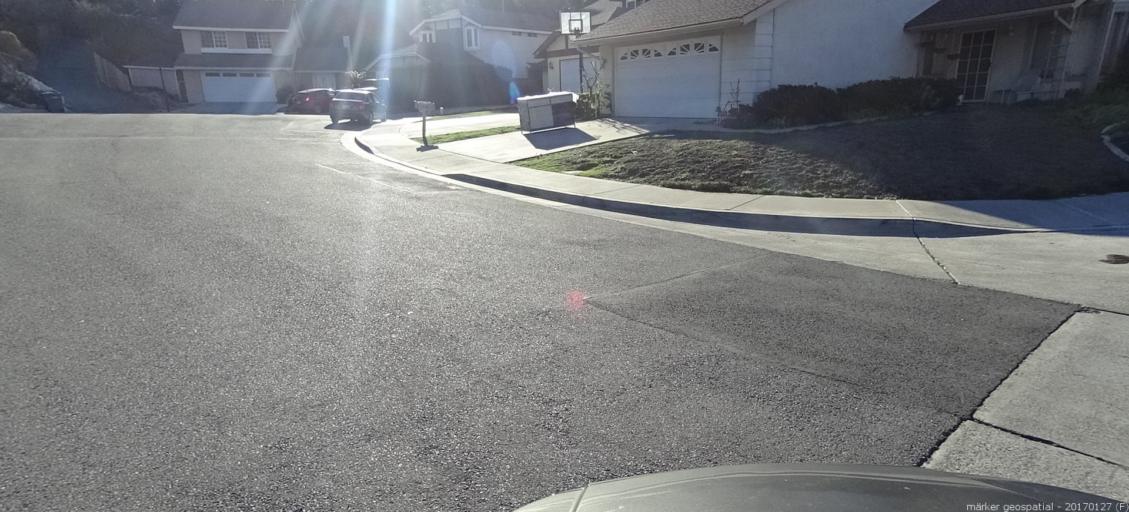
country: US
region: California
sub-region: Orange County
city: Foothill Ranch
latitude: 33.6569
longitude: -117.6546
